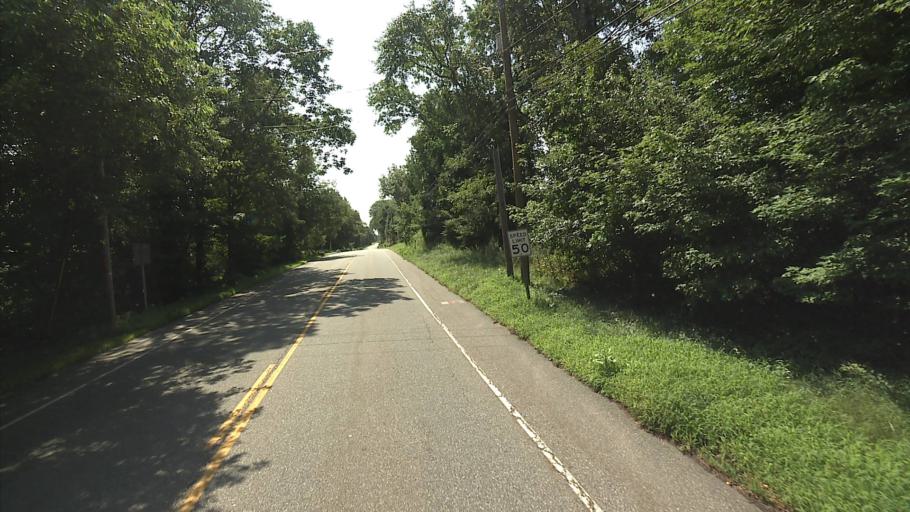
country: US
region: Connecticut
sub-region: New London County
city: Colchester
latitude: 41.5225
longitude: -72.2581
